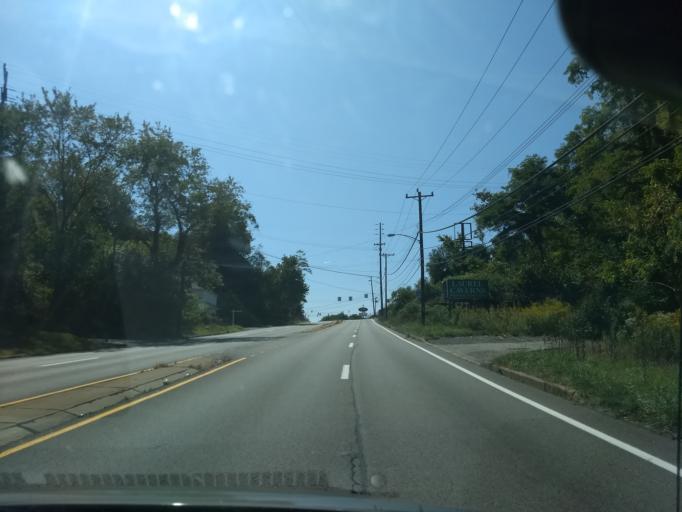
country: US
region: Pennsylvania
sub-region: Allegheny County
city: East Pittsburgh
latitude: 40.3820
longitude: -79.8281
